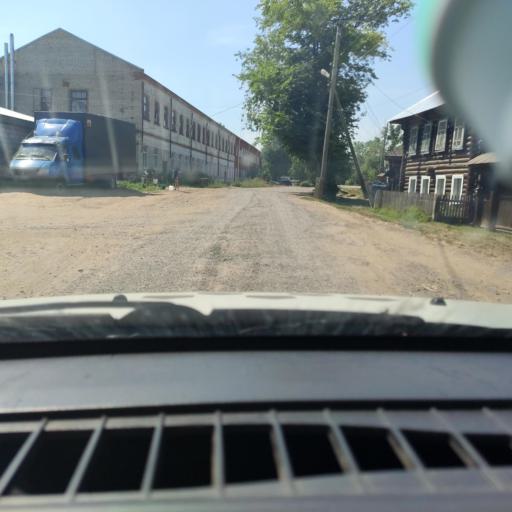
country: RU
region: Perm
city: Okhansk
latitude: 57.7226
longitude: 55.3941
